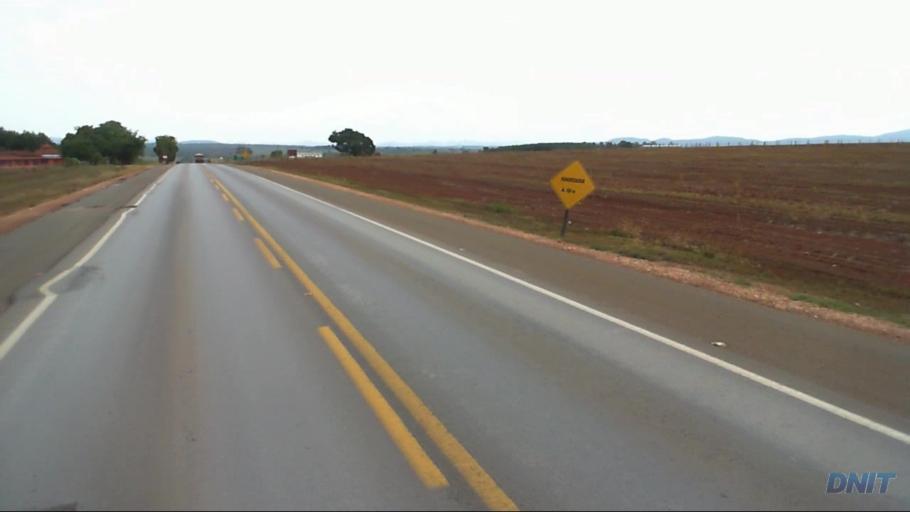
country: BR
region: Goias
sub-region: Uruacu
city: Uruacu
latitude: -14.6398
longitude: -49.1729
